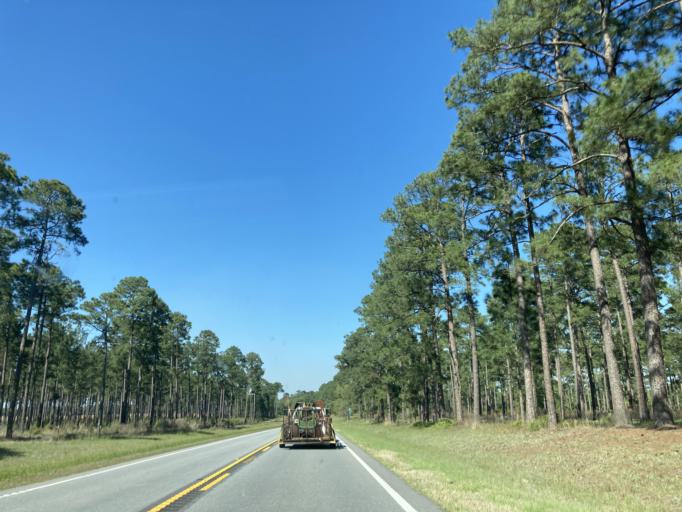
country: US
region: Georgia
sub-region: Baker County
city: Newton
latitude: 31.3675
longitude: -84.2890
